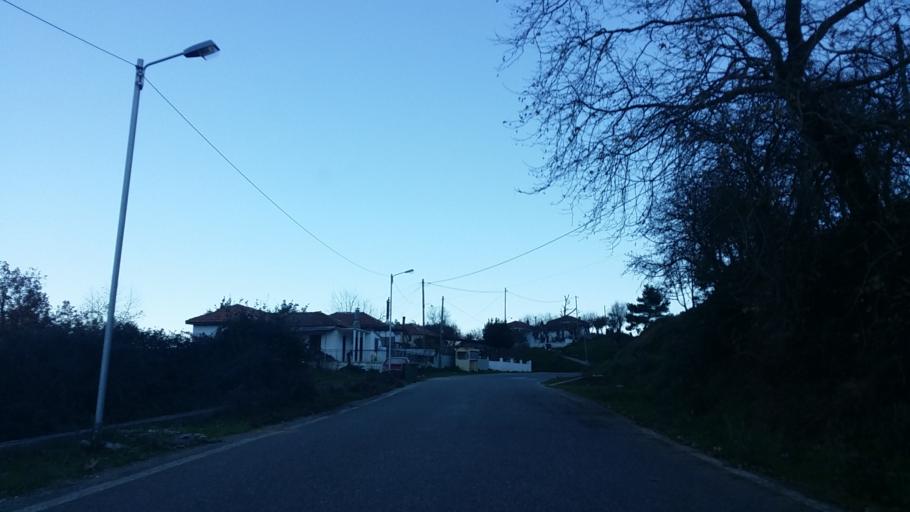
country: GR
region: West Greece
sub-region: Nomos Aitolias kai Akarnanias
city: Sardinia
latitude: 38.8661
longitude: 21.2940
